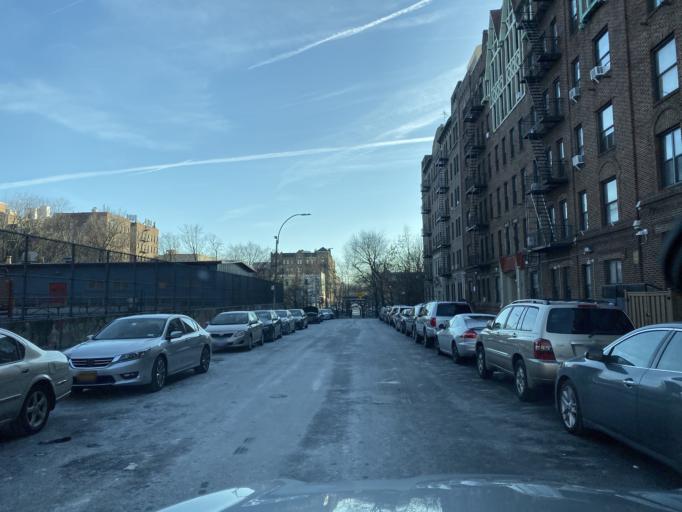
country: US
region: New York
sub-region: Kings County
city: Brooklyn
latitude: 40.6684
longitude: -73.9611
